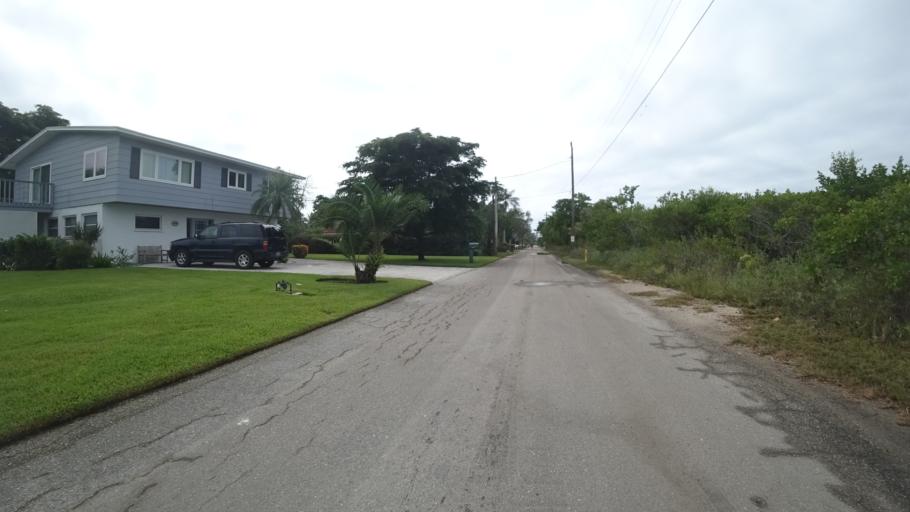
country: US
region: Florida
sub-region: Manatee County
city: Longboat Key
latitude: 27.4315
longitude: -82.6724
